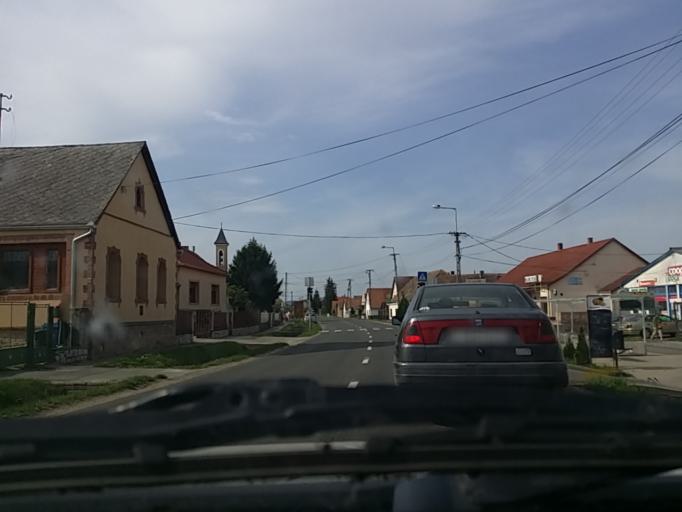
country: HU
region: Baranya
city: Kozarmisleny
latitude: 45.9488
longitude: 18.2377
